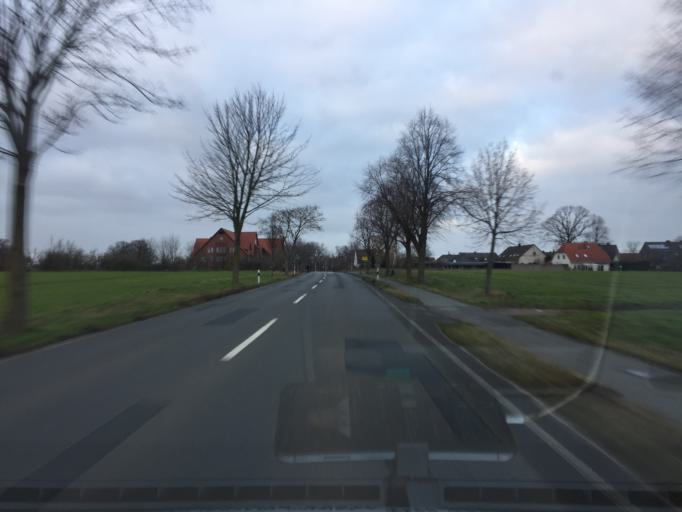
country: DE
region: Lower Saxony
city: Garbsen
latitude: 52.4529
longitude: 9.5262
